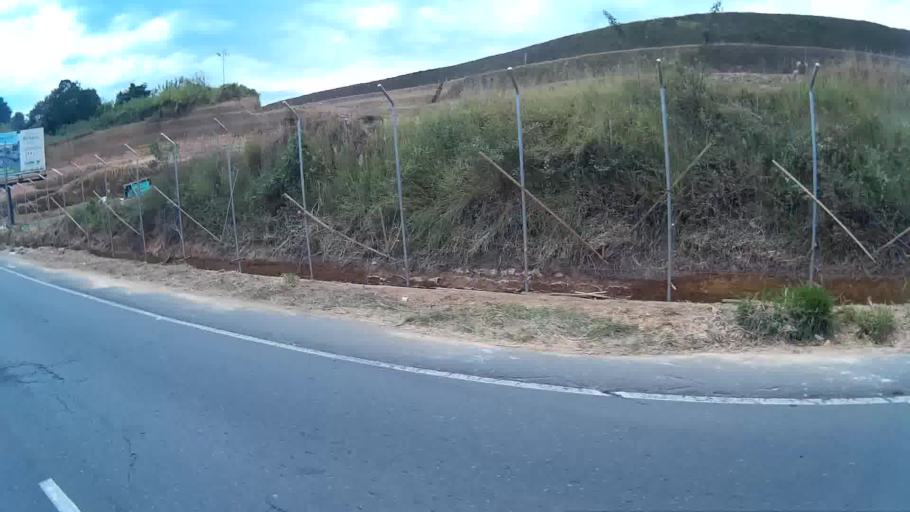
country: CO
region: Risaralda
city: Pereira
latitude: 4.8105
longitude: -75.7402
